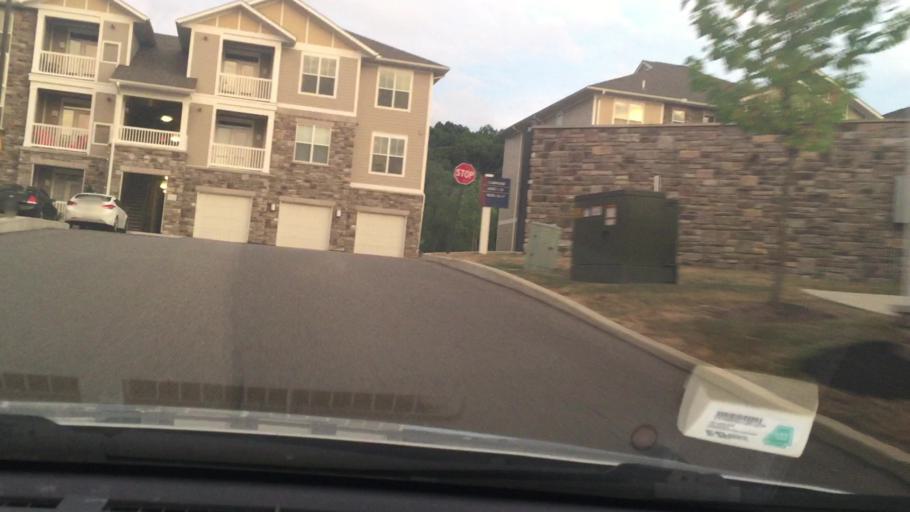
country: US
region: Pennsylvania
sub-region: Allegheny County
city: Bradford Woods
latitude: 40.6535
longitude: -80.0871
